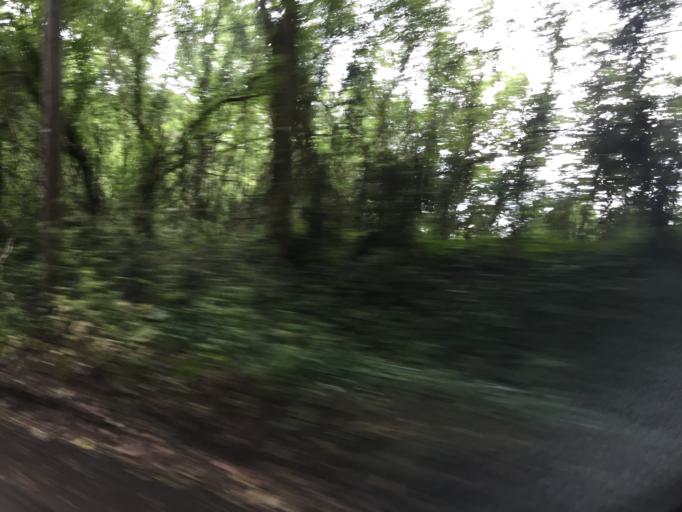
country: GB
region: England
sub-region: Wiltshire
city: Hankerton
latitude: 51.6440
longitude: -2.0136
